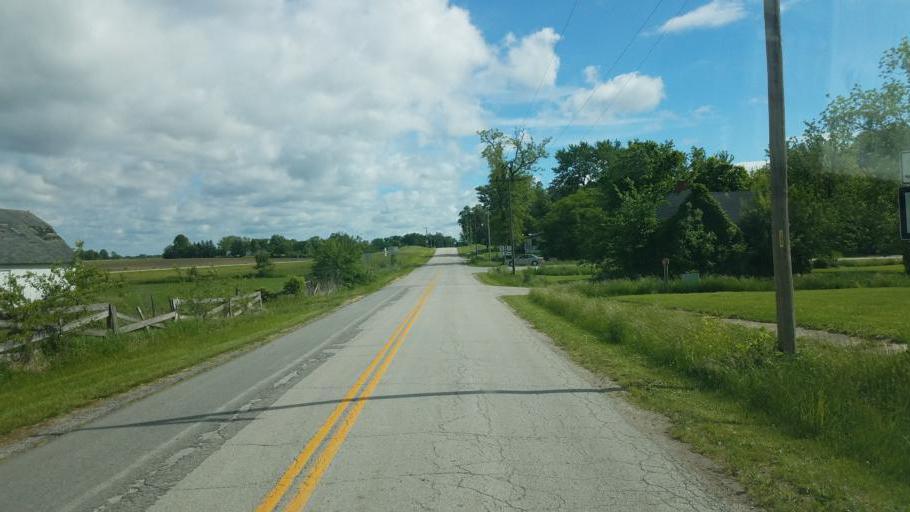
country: US
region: Missouri
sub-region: Mercer County
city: Princeton
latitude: 40.3300
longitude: -93.7971
